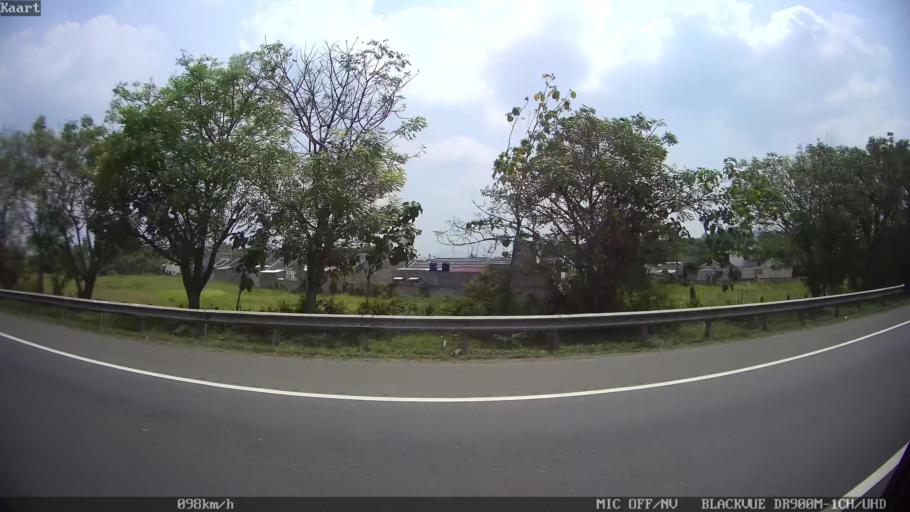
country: ID
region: Banten
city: Serang
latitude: -6.0675
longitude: 106.1264
